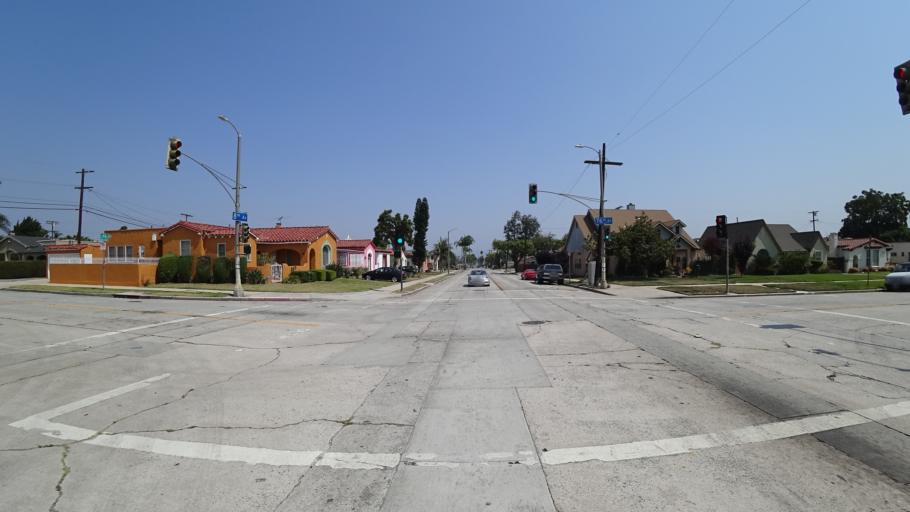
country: US
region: California
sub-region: Los Angeles County
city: Inglewood
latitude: 33.9708
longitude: -118.3265
